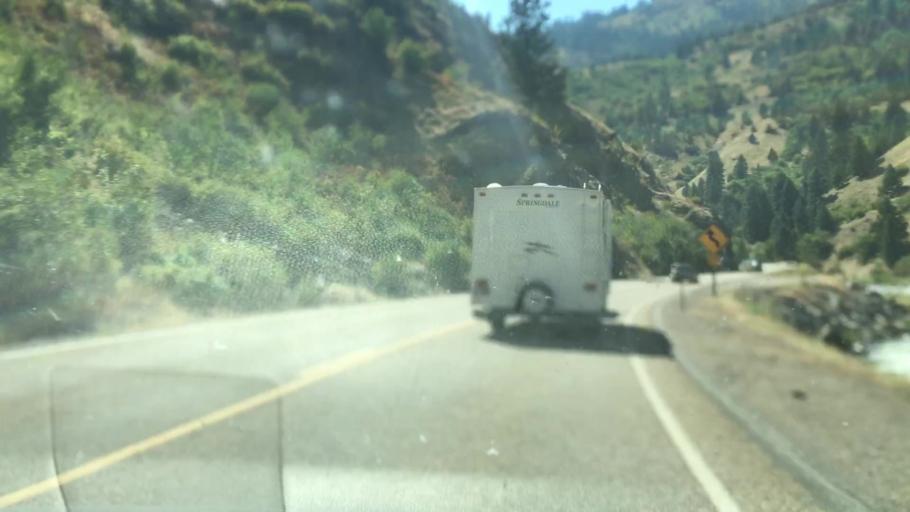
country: US
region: Idaho
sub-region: Boise County
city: Idaho City
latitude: 44.0895
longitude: -116.1078
